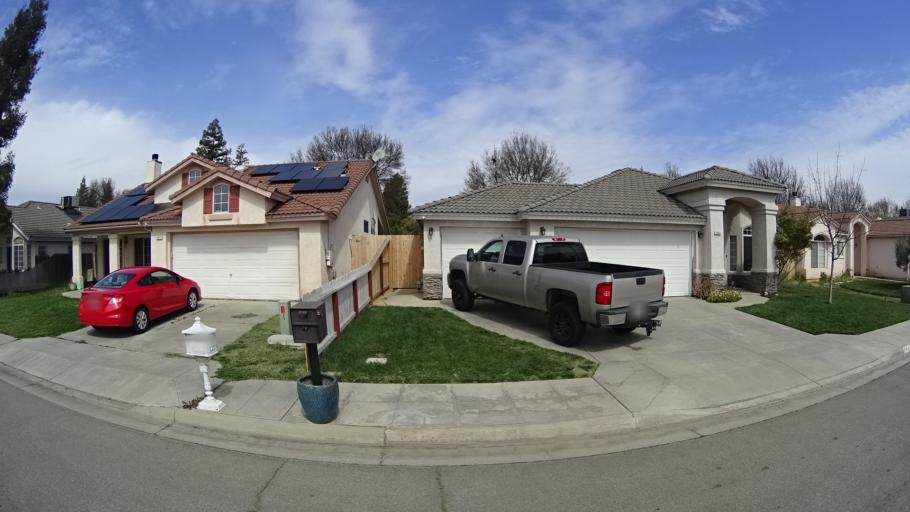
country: US
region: California
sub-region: Fresno County
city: Biola
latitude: 36.8438
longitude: -119.8898
